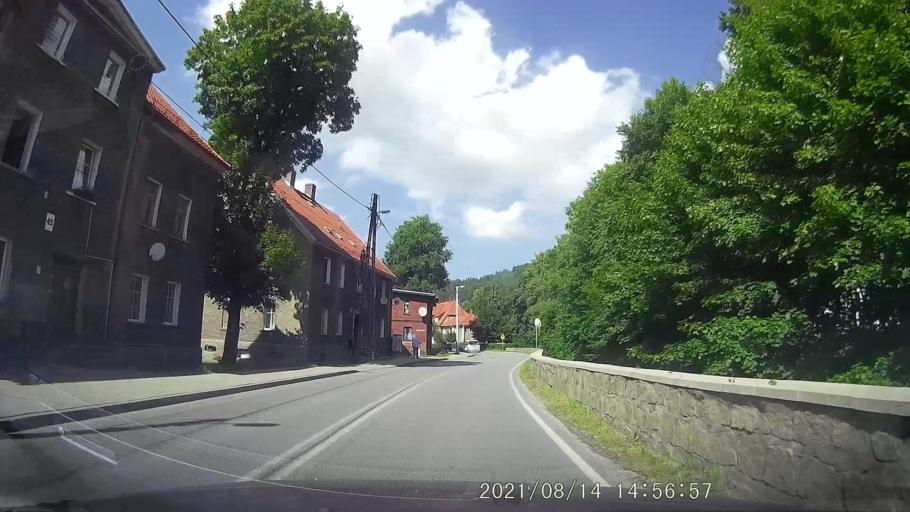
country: PL
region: Lower Silesian Voivodeship
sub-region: Powiat walbrzyski
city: Gluszyca
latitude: 50.6939
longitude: 16.3685
